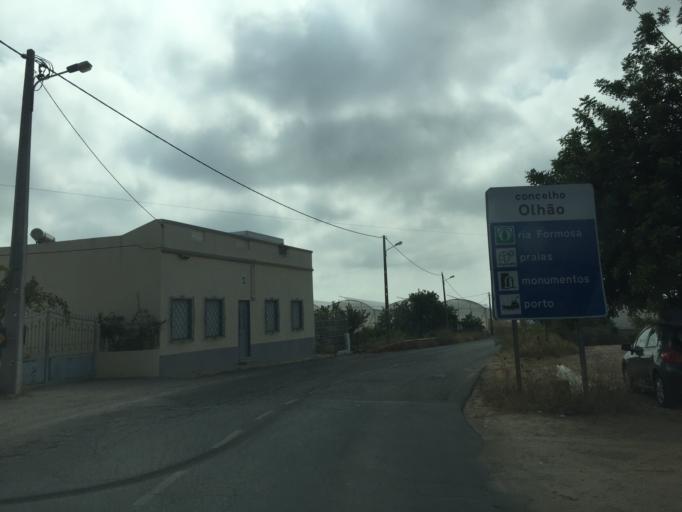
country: PT
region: Faro
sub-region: Olhao
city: Olhao
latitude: 37.0714
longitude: -7.8838
